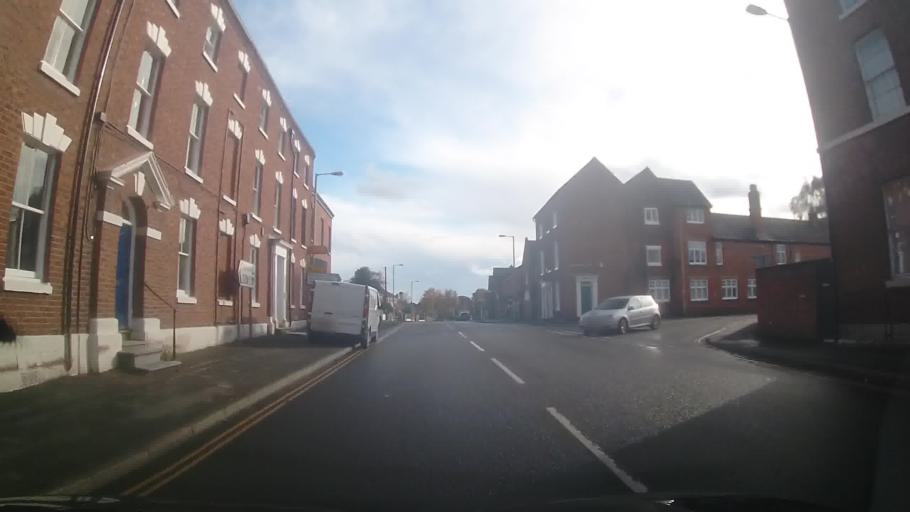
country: GB
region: England
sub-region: Shropshire
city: Whitchurch
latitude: 52.9661
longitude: -2.6813
